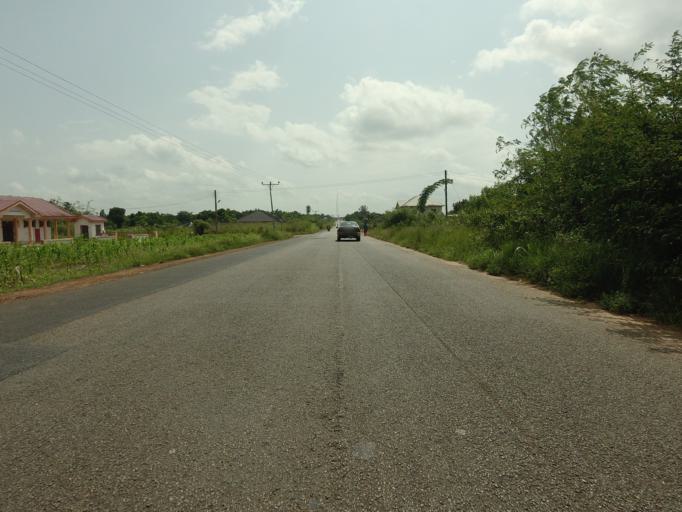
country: TG
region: Maritime
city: Lome
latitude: 6.2289
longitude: 1.0131
